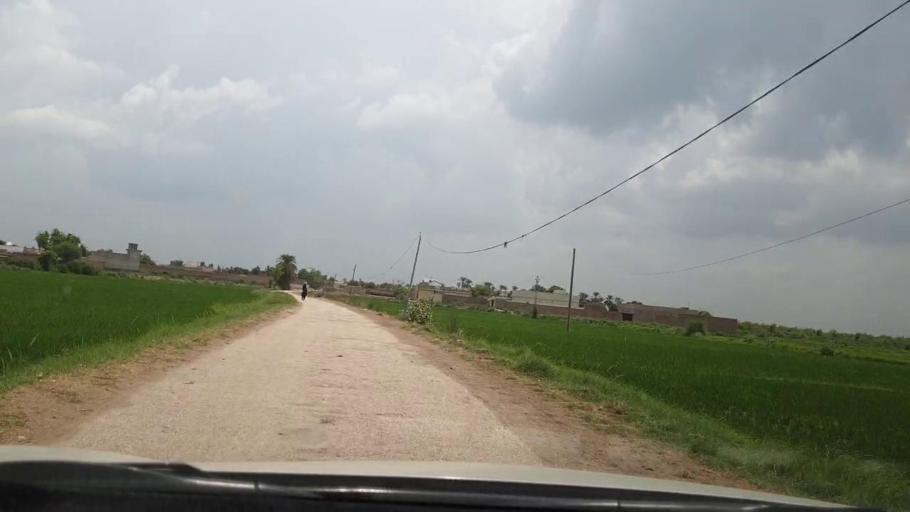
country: PK
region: Sindh
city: Goth Garelo
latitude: 27.4216
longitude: 68.1132
